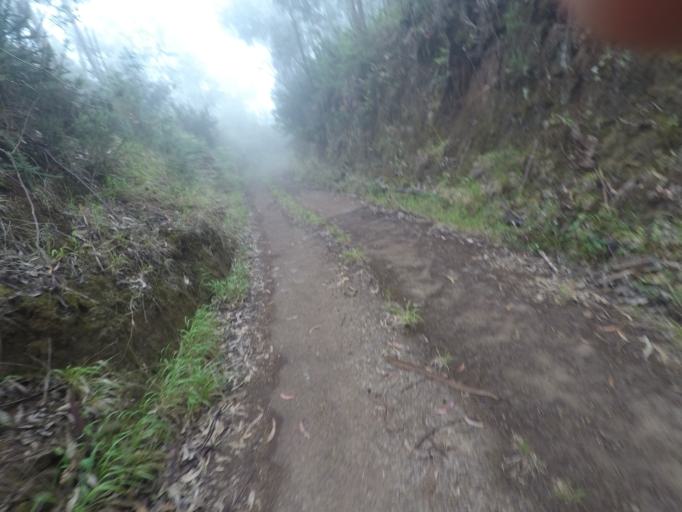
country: PT
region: Madeira
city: Ponta do Sol
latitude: 32.7143
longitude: -17.0937
